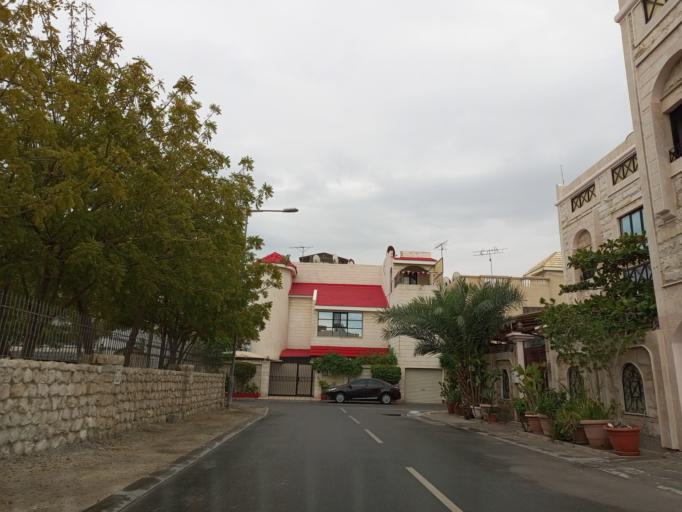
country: BH
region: Muharraq
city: Al Hadd
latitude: 26.2578
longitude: 50.6409
